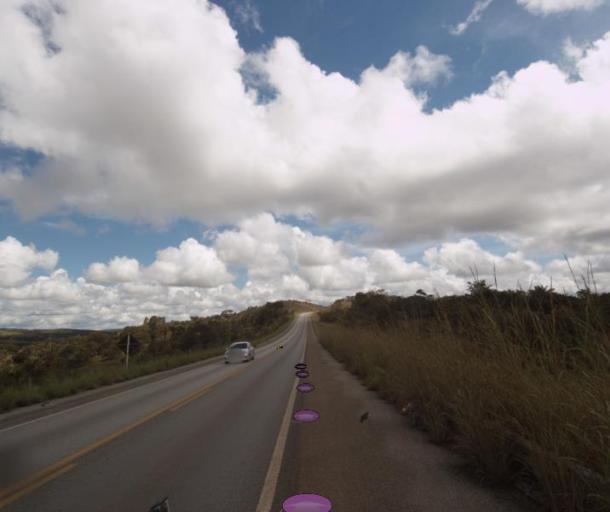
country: BR
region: Goias
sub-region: Pirenopolis
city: Pirenopolis
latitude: -15.7711
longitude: -48.5501
